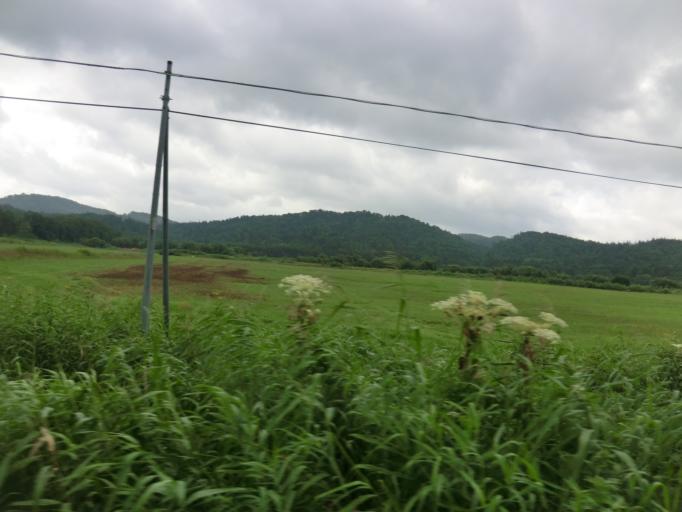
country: JP
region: Hokkaido
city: Nayoro
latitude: 44.2177
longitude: 142.1561
